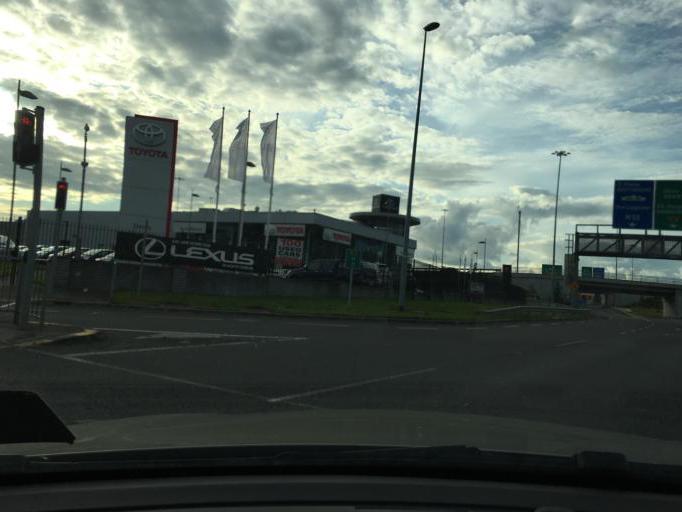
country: IE
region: Leinster
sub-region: Dublin City
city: Finglas
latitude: 53.4021
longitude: -6.3098
